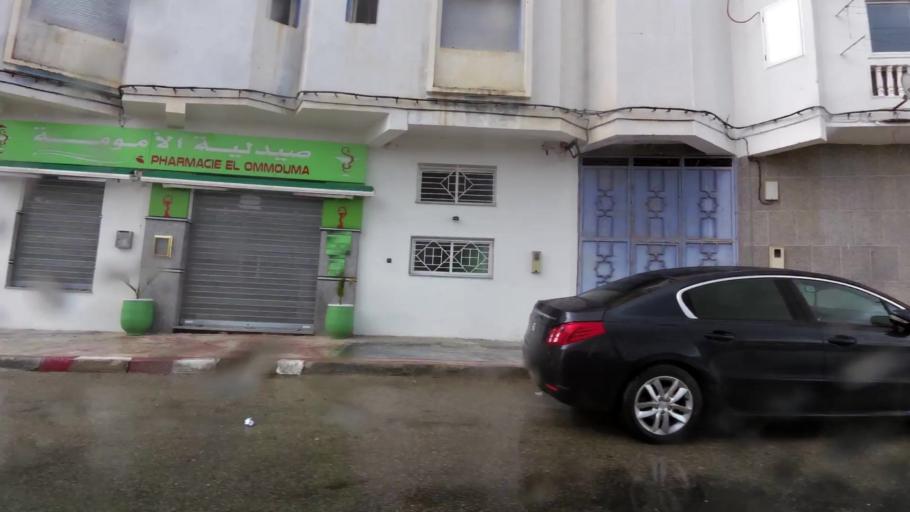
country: MA
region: Tanger-Tetouan
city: Chefchaouene
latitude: 35.1666
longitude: -5.2737
